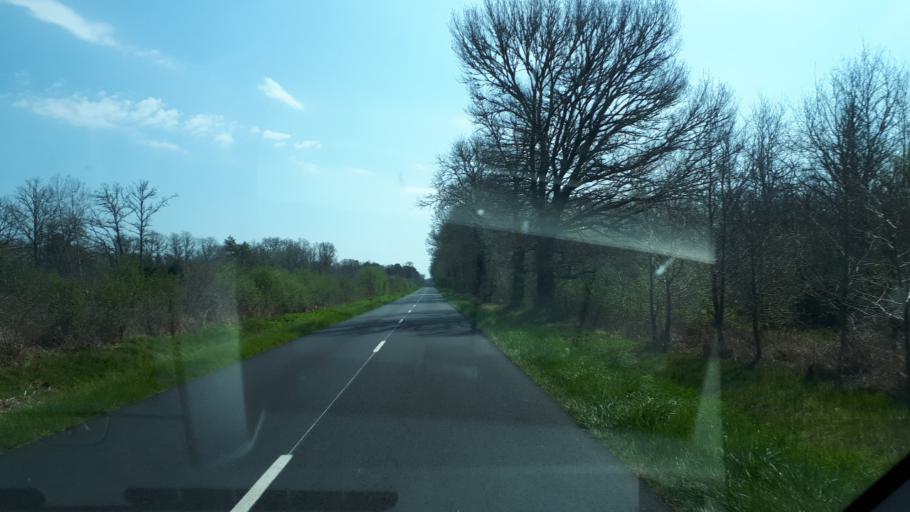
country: FR
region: Centre
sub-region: Departement du Loir-et-Cher
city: Selles-Saint-Denis
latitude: 47.3468
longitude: 1.8778
